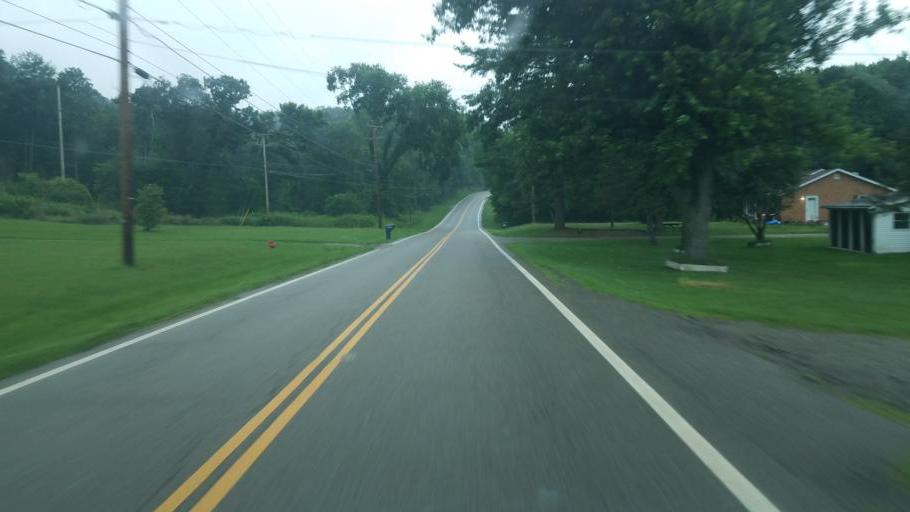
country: US
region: Ohio
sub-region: Tuscarawas County
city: Rockford
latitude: 40.4316
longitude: -81.1964
